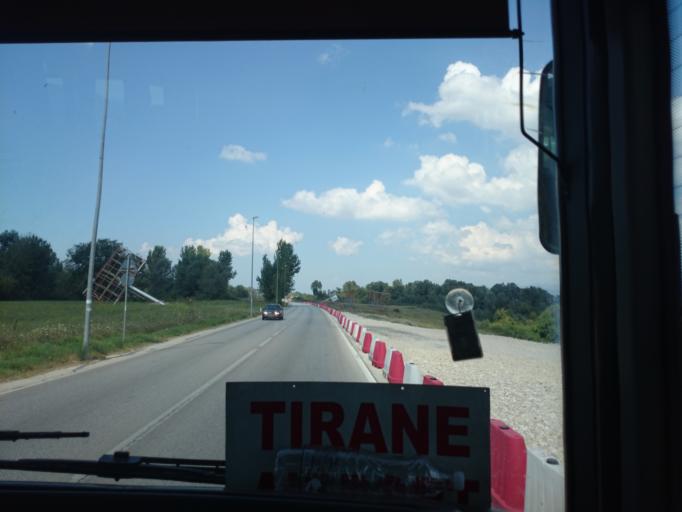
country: AL
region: Tirane
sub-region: Rrethi i Tiranes
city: Berxull
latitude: 41.4090
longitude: 19.7037
